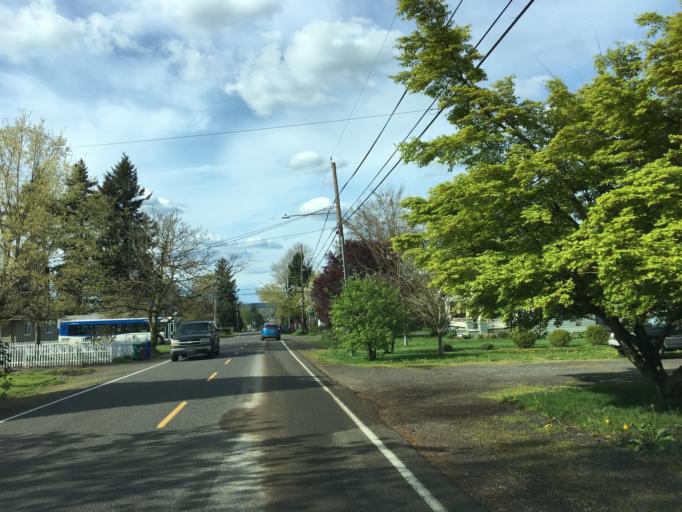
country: US
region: Oregon
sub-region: Multnomah County
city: Lents
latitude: 45.5510
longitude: -122.5547
